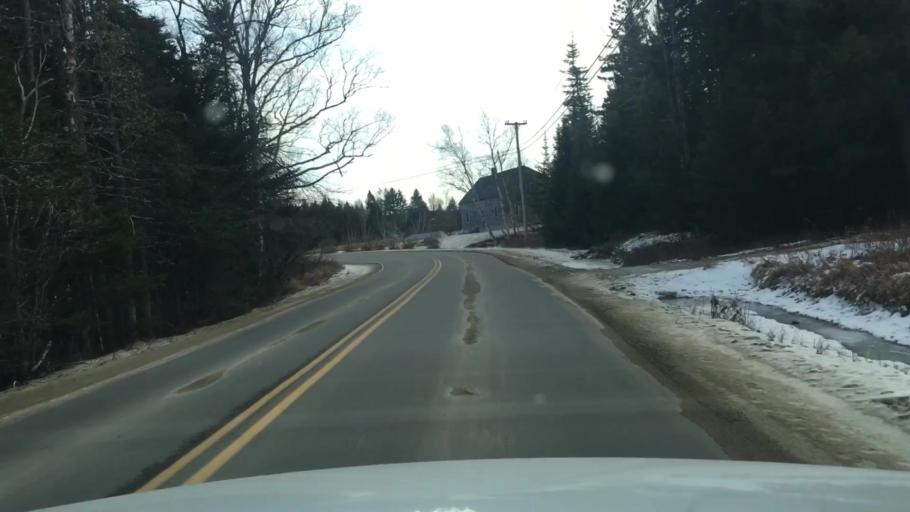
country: US
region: Maine
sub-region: Washington County
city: Jonesport
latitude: 44.6102
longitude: -67.6019
